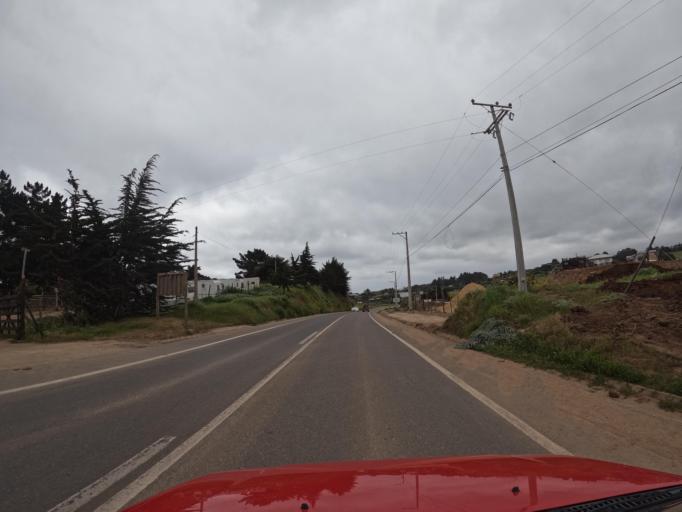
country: CL
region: O'Higgins
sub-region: Provincia de Colchagua
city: Santa Cruz
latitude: -34.4328
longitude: -72.0336
